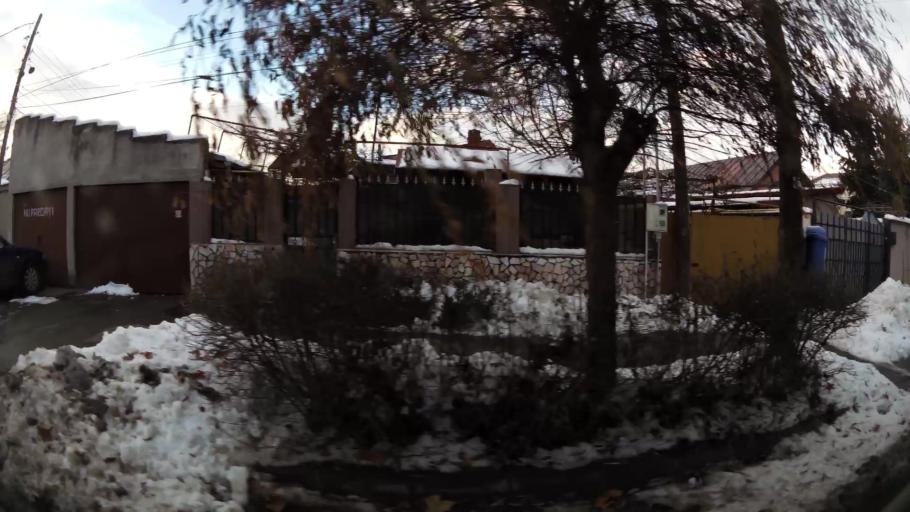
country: RO
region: Ilfov
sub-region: Comuna Fundeni-Dobroesti
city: Fundeni
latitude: 44.4461
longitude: 26.1697
